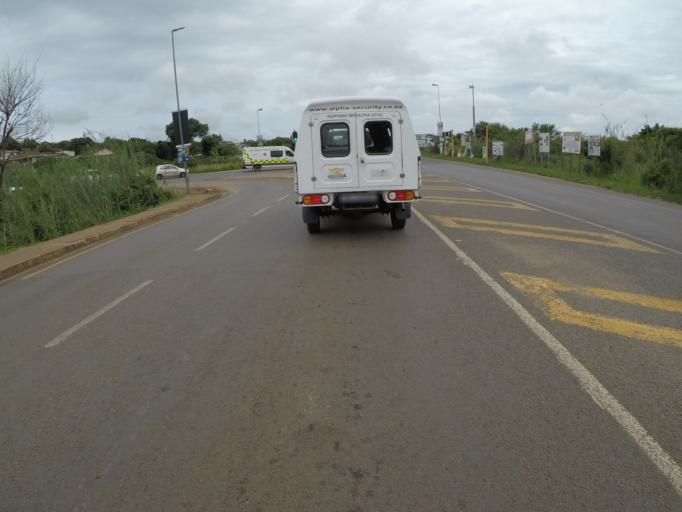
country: ZA
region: KwaZulu-Natal
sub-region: uThungulu District Municipality
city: Empangeni
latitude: -28.7766
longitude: 31.8759
